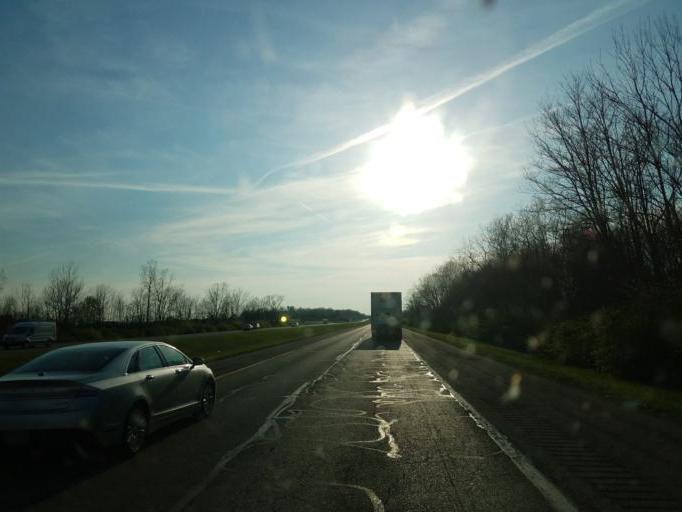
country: US
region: Ohio
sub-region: Warren County
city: Morrow
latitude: 39.4138
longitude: -84.1432
